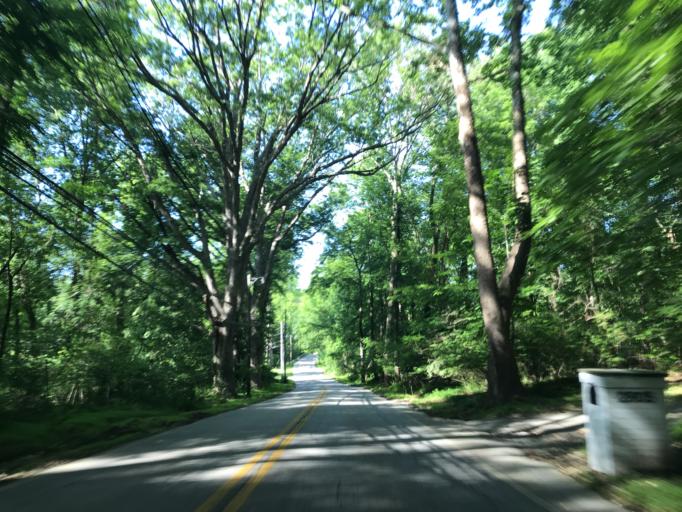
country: US
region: Maryland
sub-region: Baltimore County
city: Garrison
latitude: 39.4345
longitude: -76.7357
